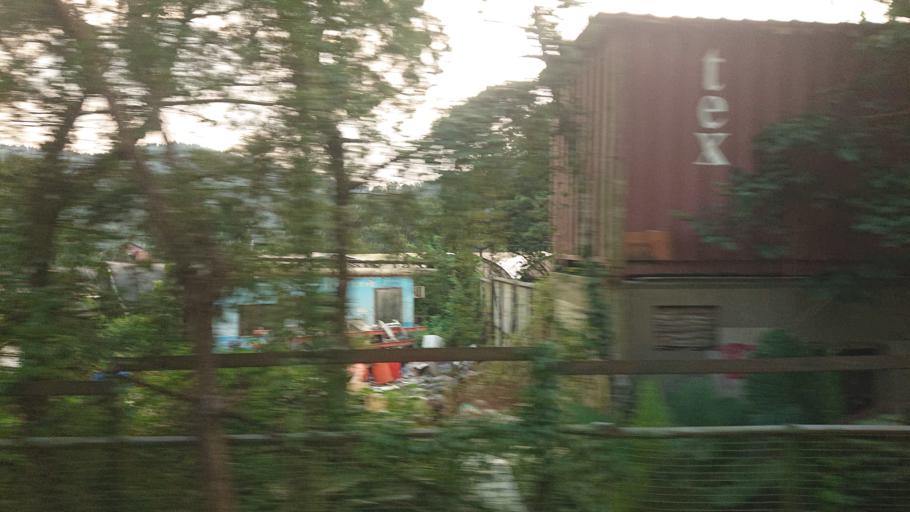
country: TW
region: Taiwan
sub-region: Nantou
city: Puli
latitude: 23.9646
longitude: 121.0011
